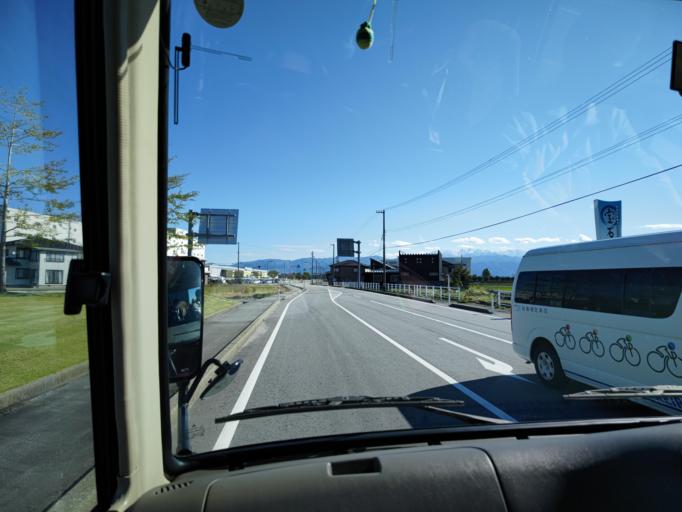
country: JP
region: Toyama
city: Nyuzen
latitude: 36.8930
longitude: 137.4307
